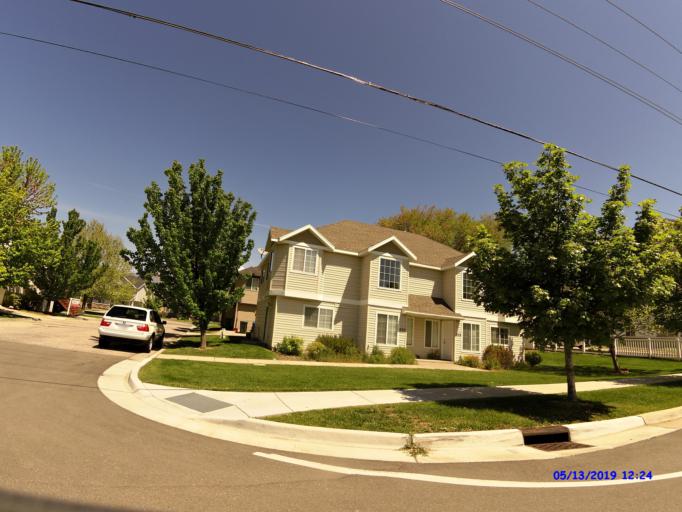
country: US
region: Utah
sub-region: Weber County
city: Harrisville
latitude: 41.2665
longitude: -111.9624
